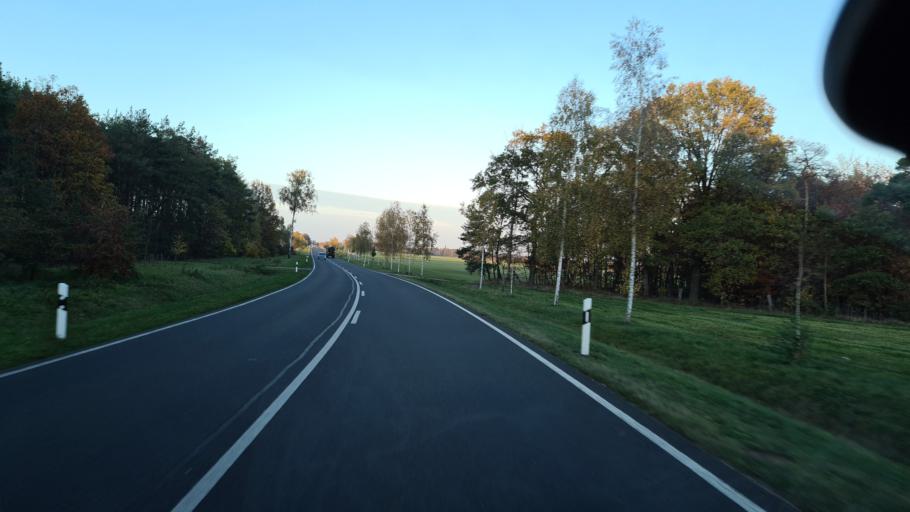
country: DE
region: Saxony
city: Schildau
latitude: 51.4809
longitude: 12.9843
